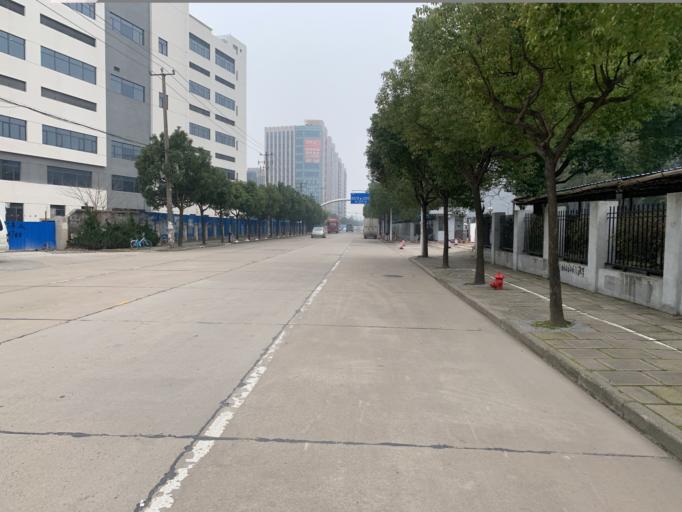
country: CN
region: Shanghai Shi
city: Huamu
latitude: 31.2488
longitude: 121.6230
